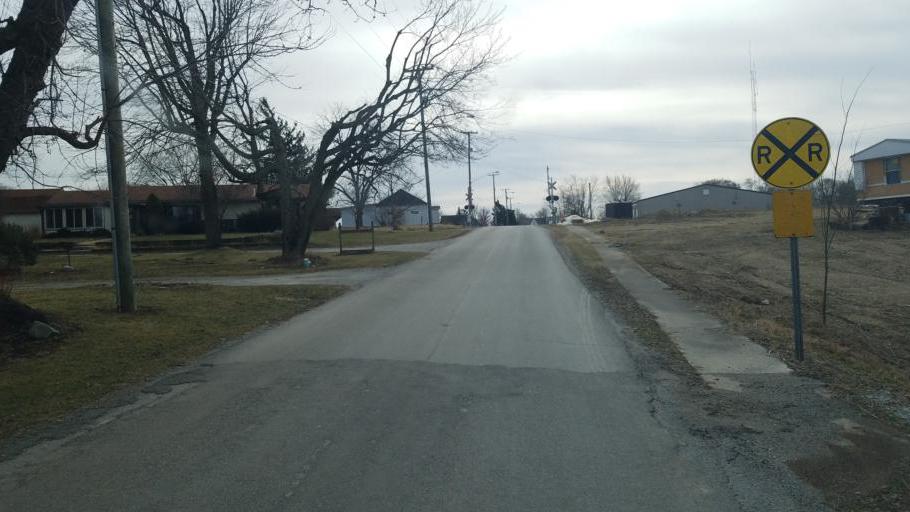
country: US
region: Ohio
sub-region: Hardin County
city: Kenton
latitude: 40.5359
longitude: -83.5155
